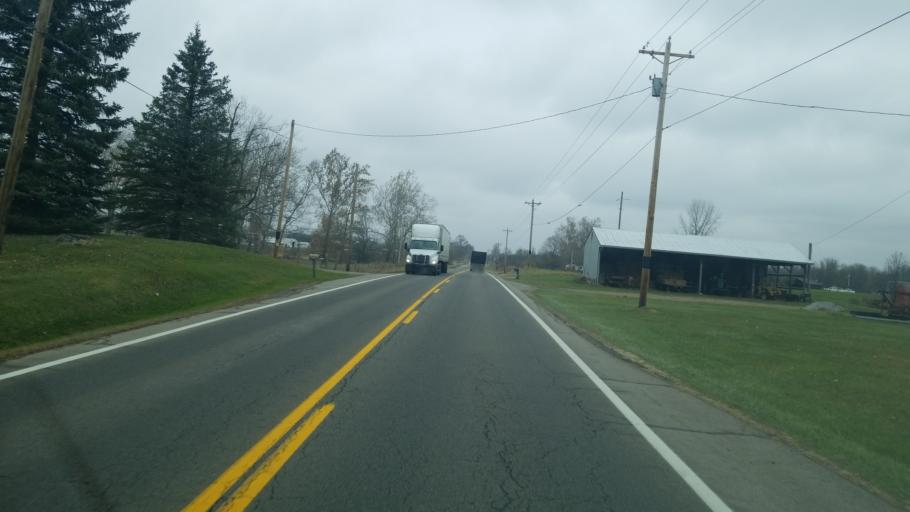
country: US
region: Ohio
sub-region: Huron County
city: Greenwich
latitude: 41.0687
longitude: -82.4869
